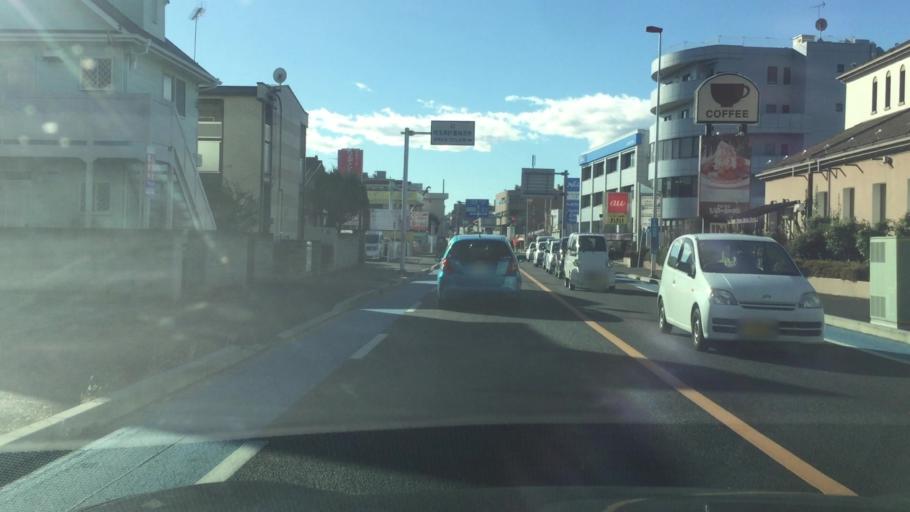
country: JP
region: Saitama
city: Yono
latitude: 35.9203
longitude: 139.6150
